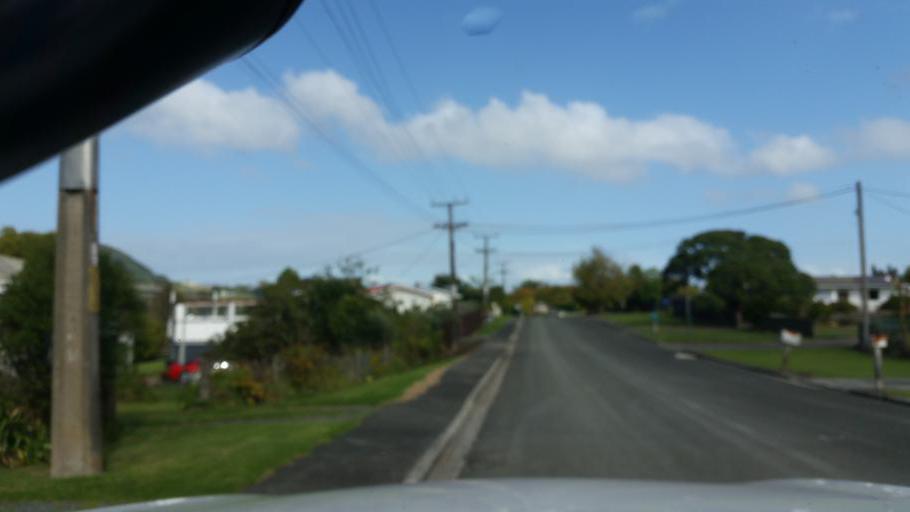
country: NZ
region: Northland
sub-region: Whangarei
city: Ruakaka
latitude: -36.1023
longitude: 174.3673
